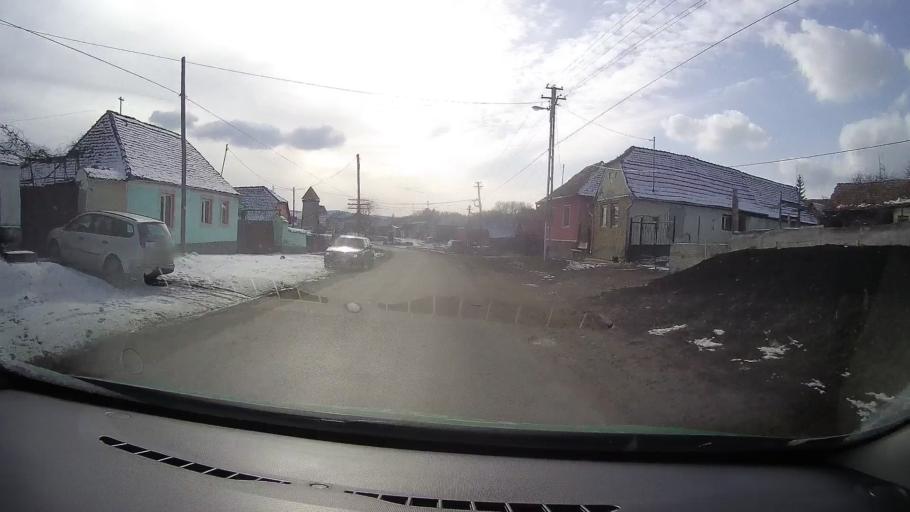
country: RO
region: Sibiu
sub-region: Comuna Bradeni
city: Bradeni
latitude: 46.0615
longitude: 24.7900
